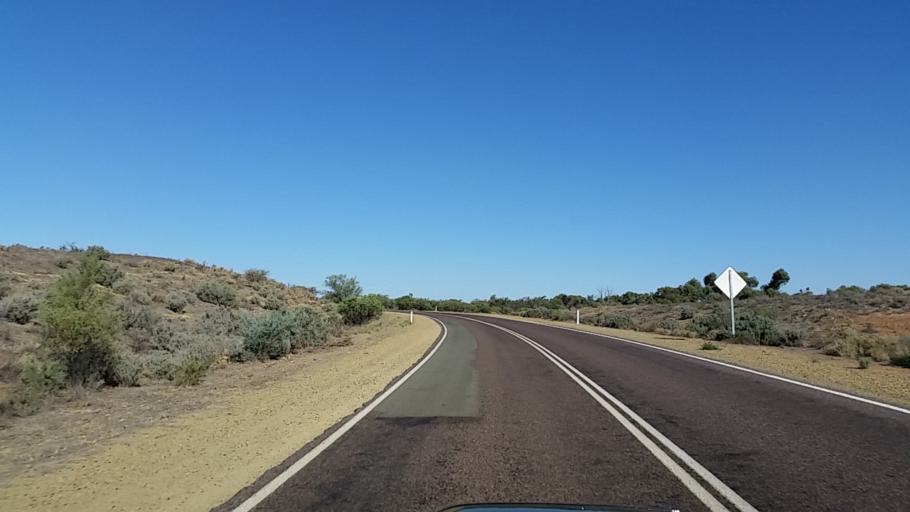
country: AU
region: South Australia
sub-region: Flinders Ranges
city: Quorn
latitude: -32.3344
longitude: 138.4743
